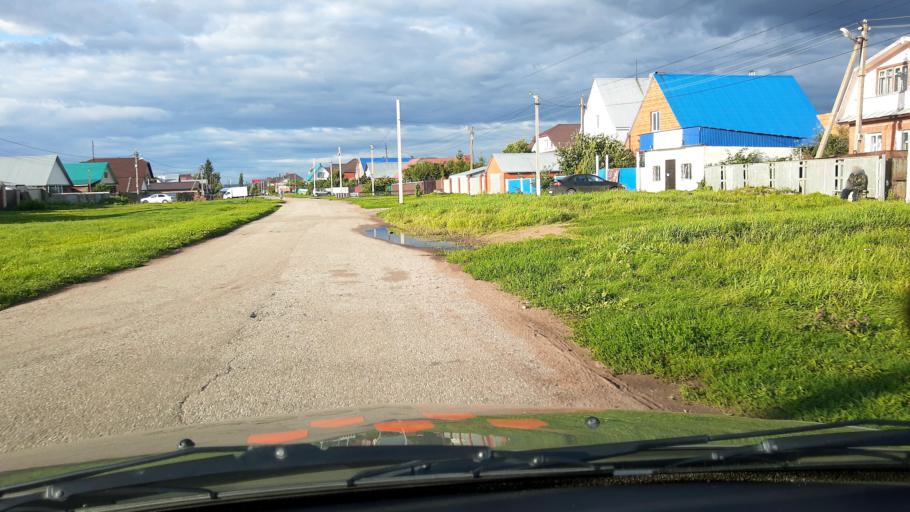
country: RU
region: Bashkortostan
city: Ufa
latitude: 54.8353
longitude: 56.0029
